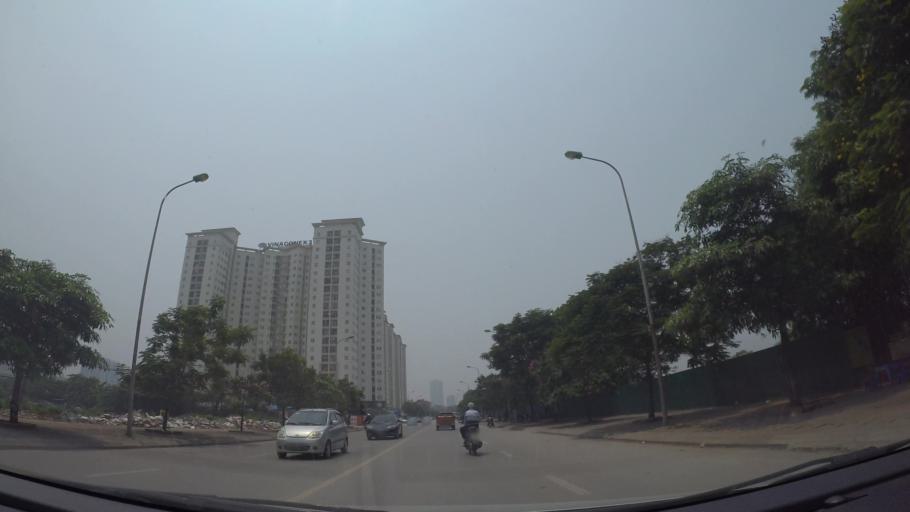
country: VN
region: Ha Noi
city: Thanh Xuan
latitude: 20.9969
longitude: 105.7796
